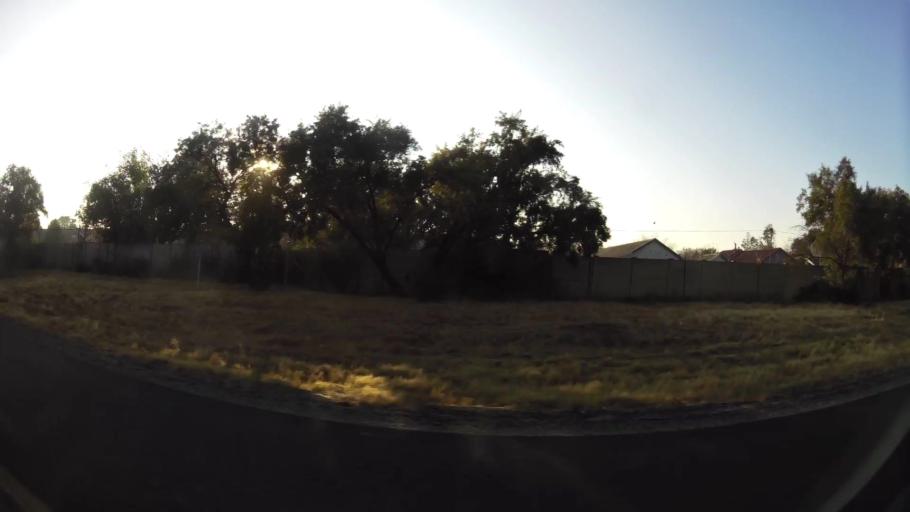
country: ZA
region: Orange Free State
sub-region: Mangaung Metropolitan Municipality
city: Bloemfontein
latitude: -29.1224
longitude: 26.1629
